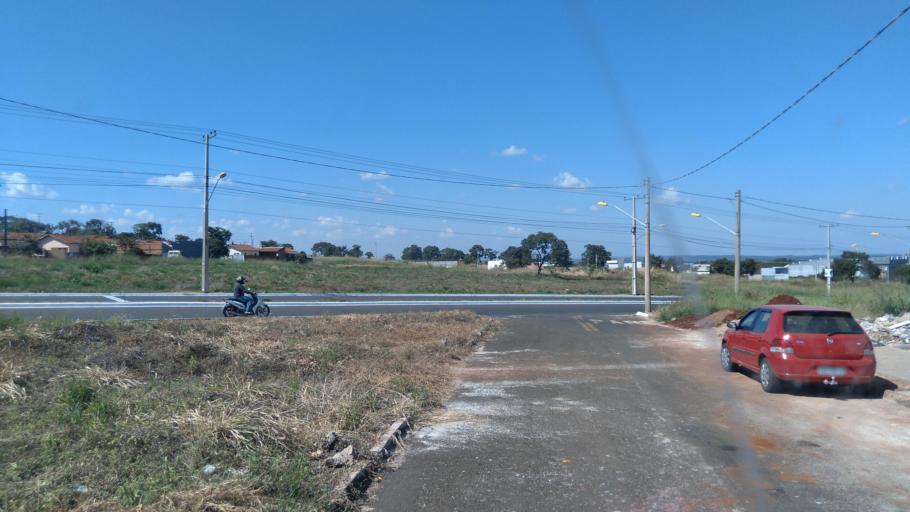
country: BR
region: Goias
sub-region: Mineiros
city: Mineiros
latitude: -17.5508
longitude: -52.5414
